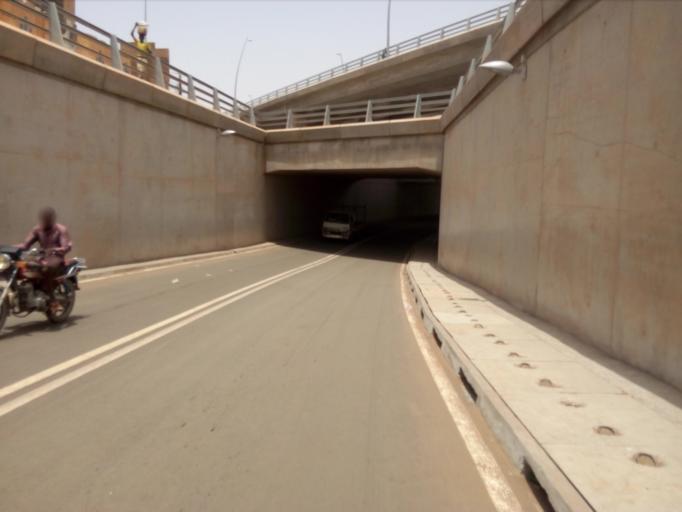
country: NE
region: Niamey
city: Niamey
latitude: 13.5205
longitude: 2.1196
